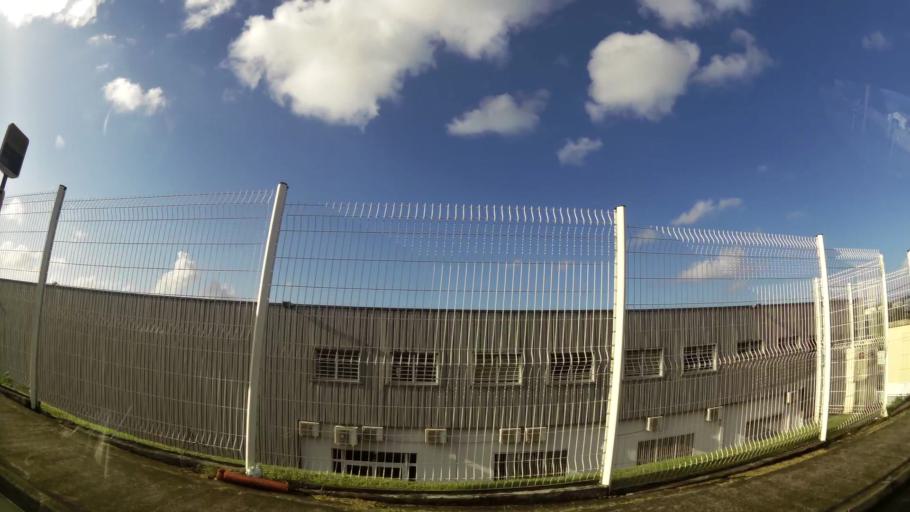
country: MQ
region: Martinique
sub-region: Martinique
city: Le Lamentin
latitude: 14.6210
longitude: -61.0191
